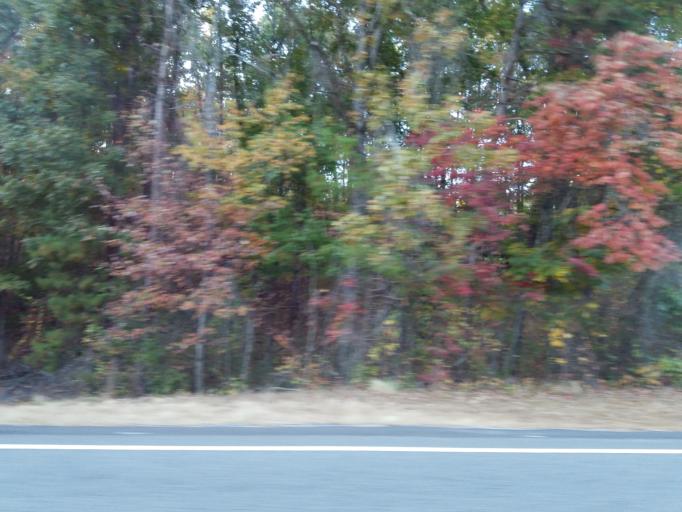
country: US
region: Georgia
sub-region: Lumpkin County
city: Dahlonega
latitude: 34.5250
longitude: -84.0313
